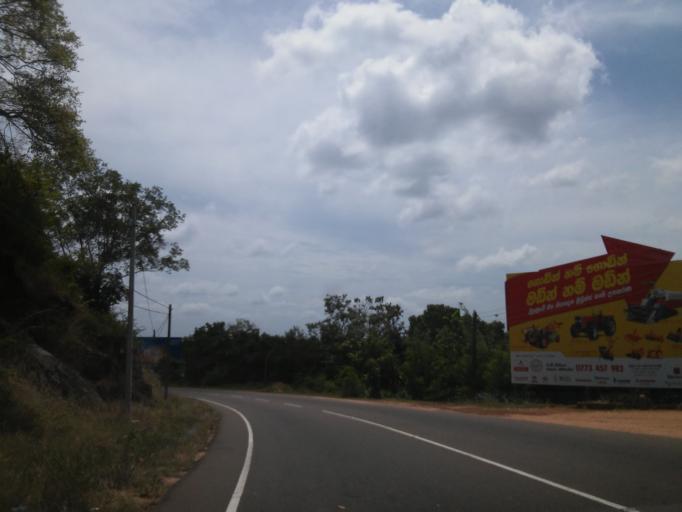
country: LK
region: Eastern Province
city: Trincomalee
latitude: 8.3466
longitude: 80.9835
